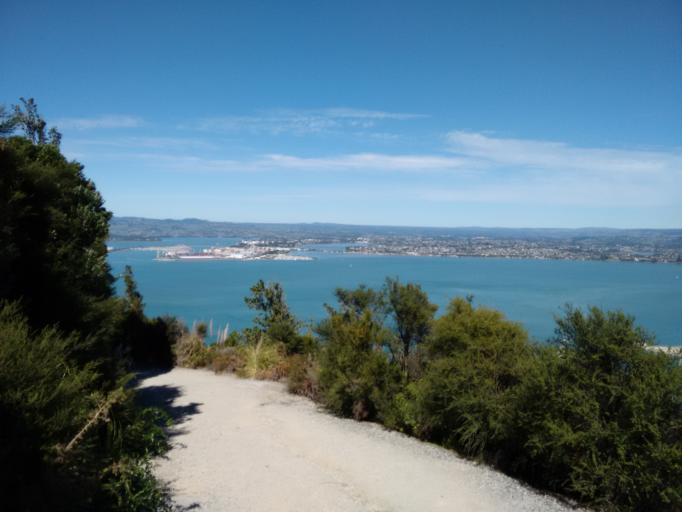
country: NZ
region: Bay of Plenty
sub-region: Tauranga City
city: Tauranga
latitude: -37.6295
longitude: 176.1702
